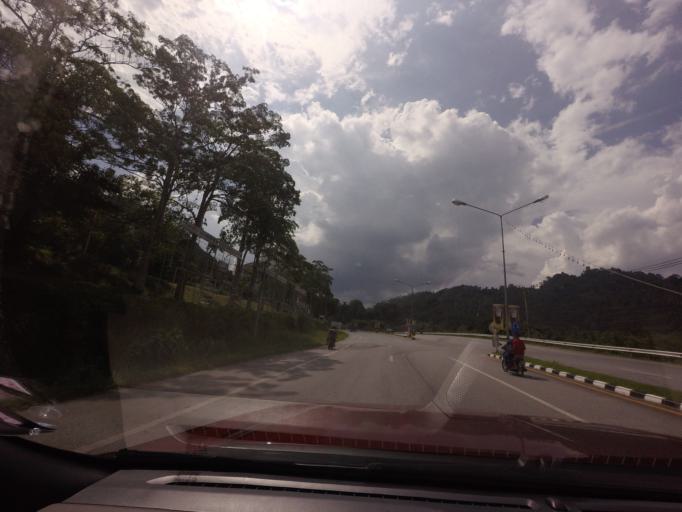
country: TH
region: Yala
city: Than To
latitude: 6.1679
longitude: 101.1809
